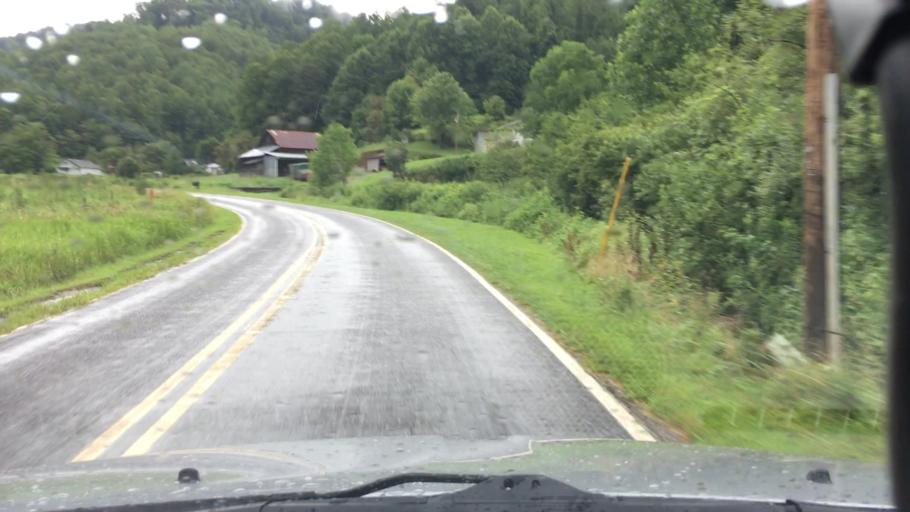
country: US
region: North Carolina
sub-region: Madison County
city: Mars Hill
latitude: 35.9120
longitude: -82.4753
